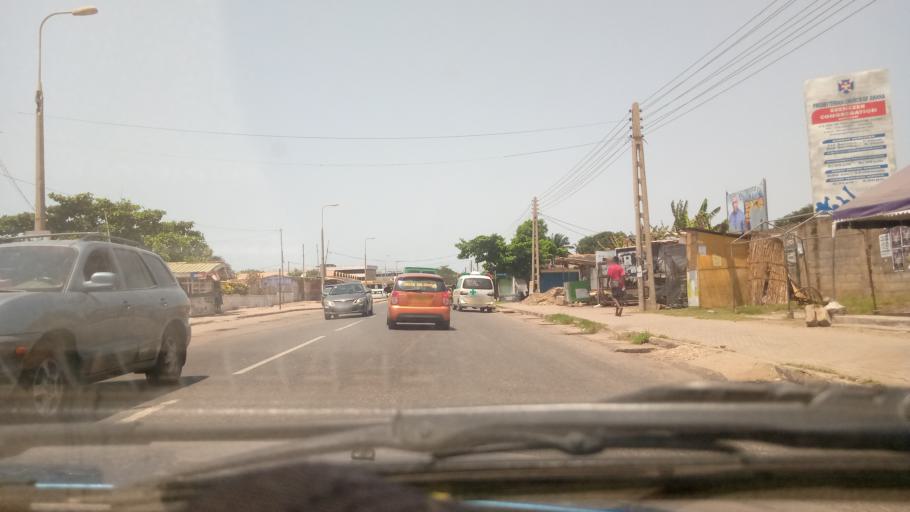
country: GH
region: Greater Accra
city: Accra
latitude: 5.5342
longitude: -0.2357
